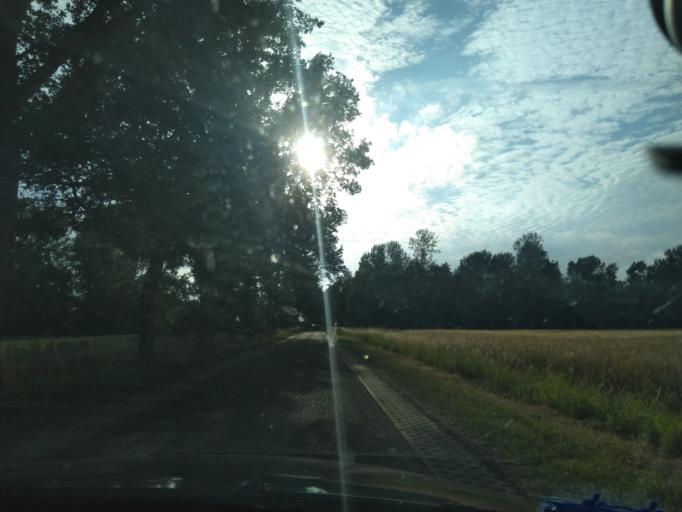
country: NL
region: Groningen
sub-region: Gemeente  Oldambt
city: Winschoten
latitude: 53.0963
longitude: 7.0850
